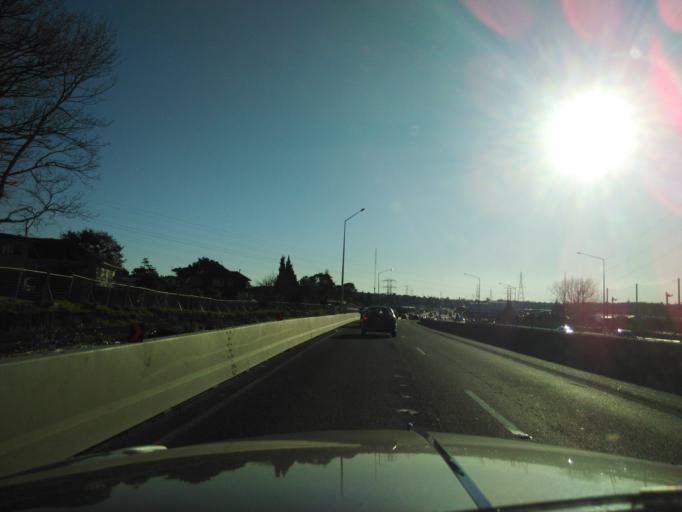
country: NZ
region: Auckland
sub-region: Auckland
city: Rosebank
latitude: -36.8550
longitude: 174.6454
